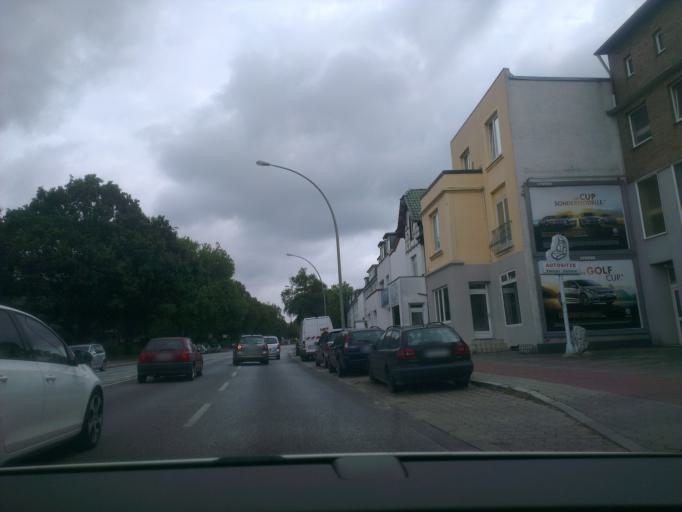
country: DE
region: Hamburg
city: Steilshoop
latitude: 53.5942
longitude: 10.0599
